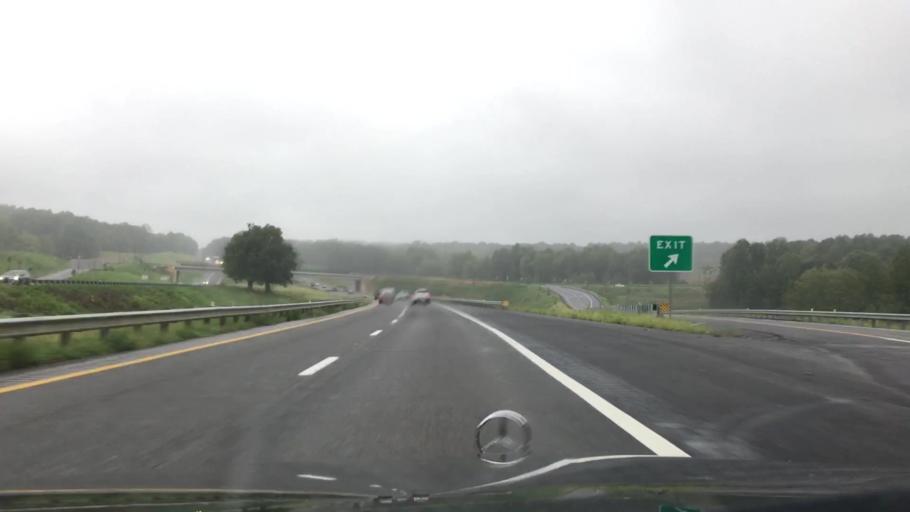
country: US
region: Virginia
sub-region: City of Lynchburg
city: Lynchburg
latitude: 37.3752
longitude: -79.1444
